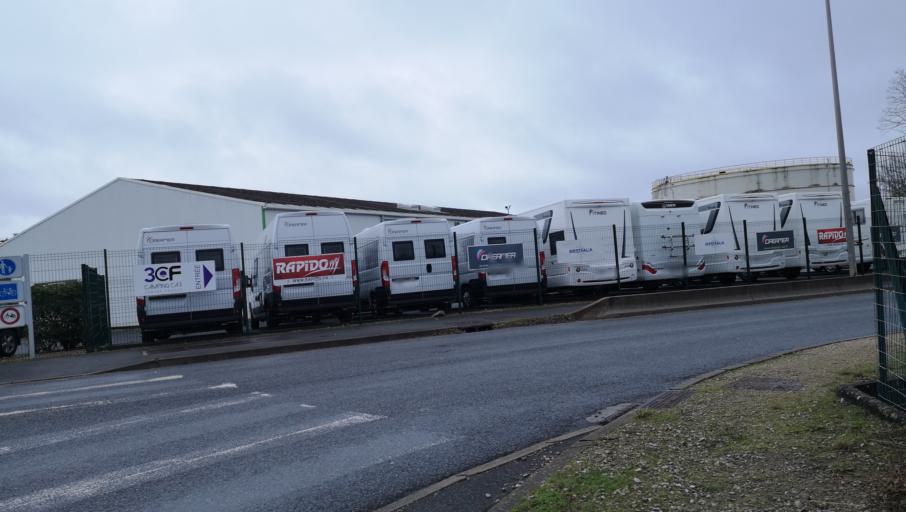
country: FR
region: Centre
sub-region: Departement du Loiret
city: Semoy
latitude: 47.9214
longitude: 1.9567
